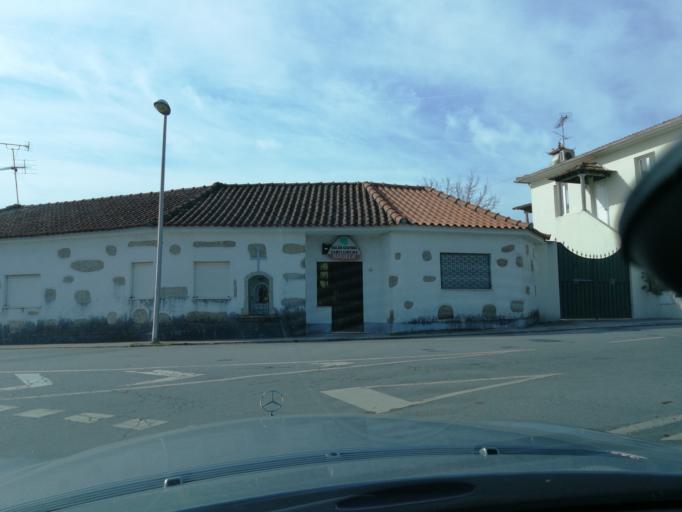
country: PT
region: Braga
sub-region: Vila Nova de Famalicao
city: Vila Nova de Famalicao
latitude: 41.4375
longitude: -8.5227
